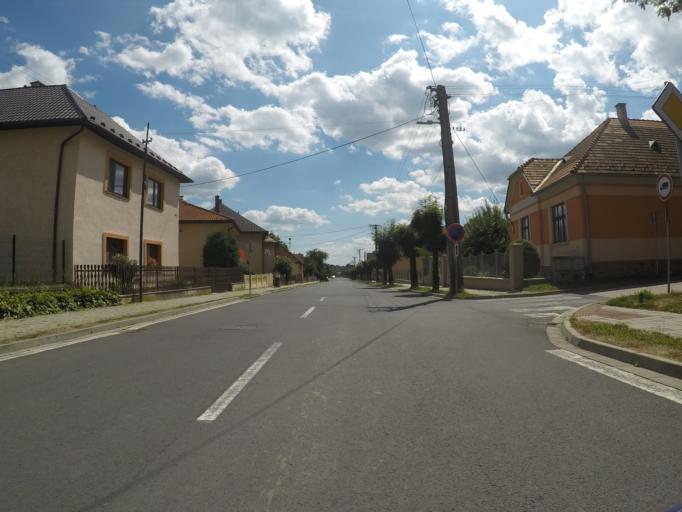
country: SK
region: Banskobystricky
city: Tisovec
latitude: 48.6791
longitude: 19.9405
